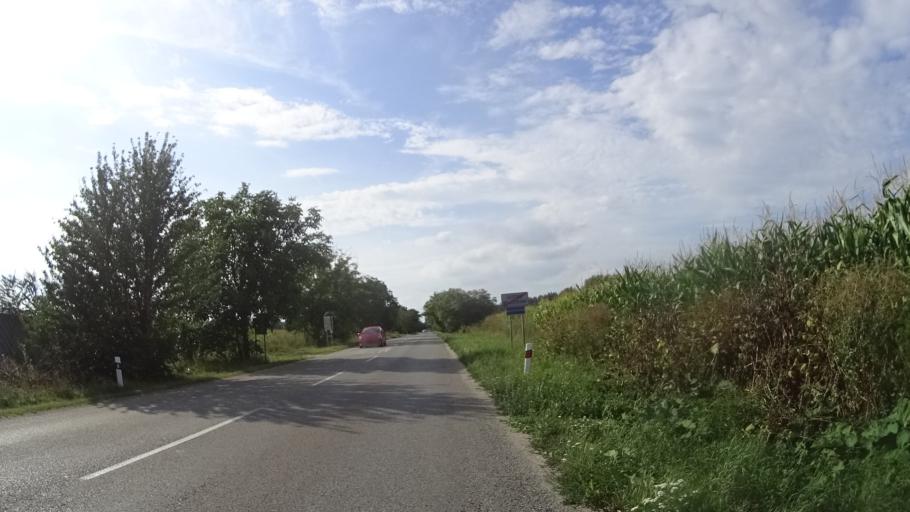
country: SK
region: Trnavsky
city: Gabcikovo
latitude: 47.9243
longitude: 17.4946
